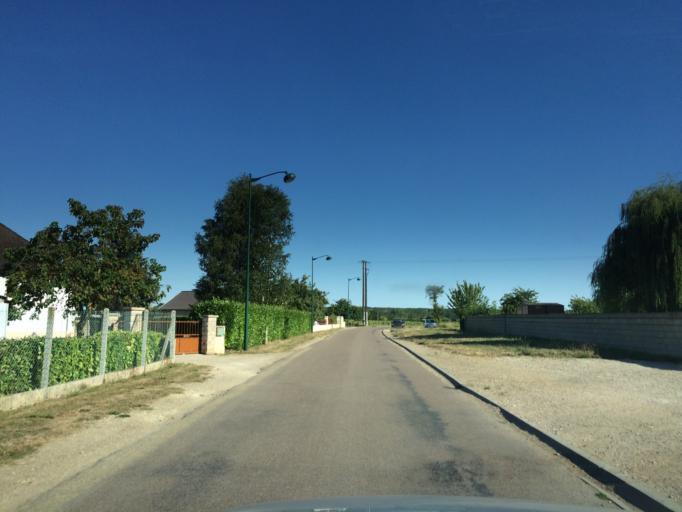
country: FR
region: Bourgogne
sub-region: Departement de l'Yonne
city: Fleury-la-Vallee
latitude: 47.9125
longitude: 3.4376
